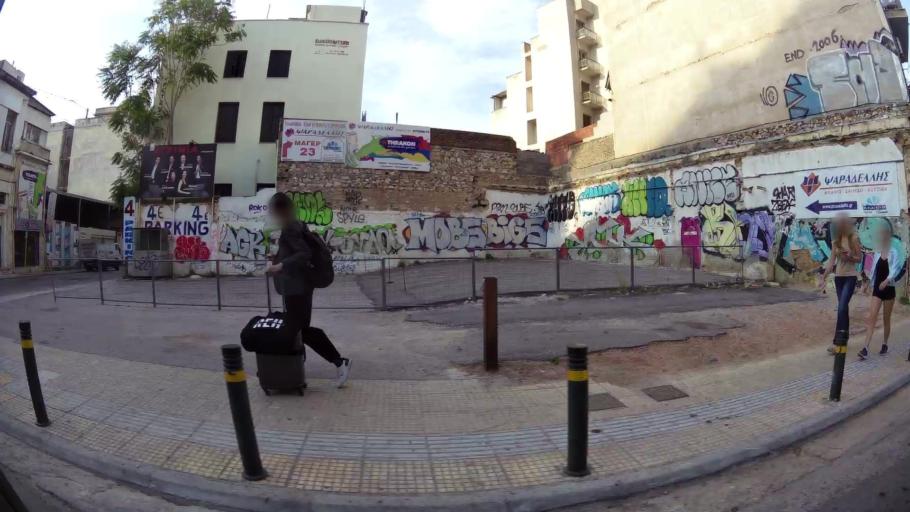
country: GR
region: Attica
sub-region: Nomarchia Athinas
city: Athens
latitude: 37.9880
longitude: 23.7257
